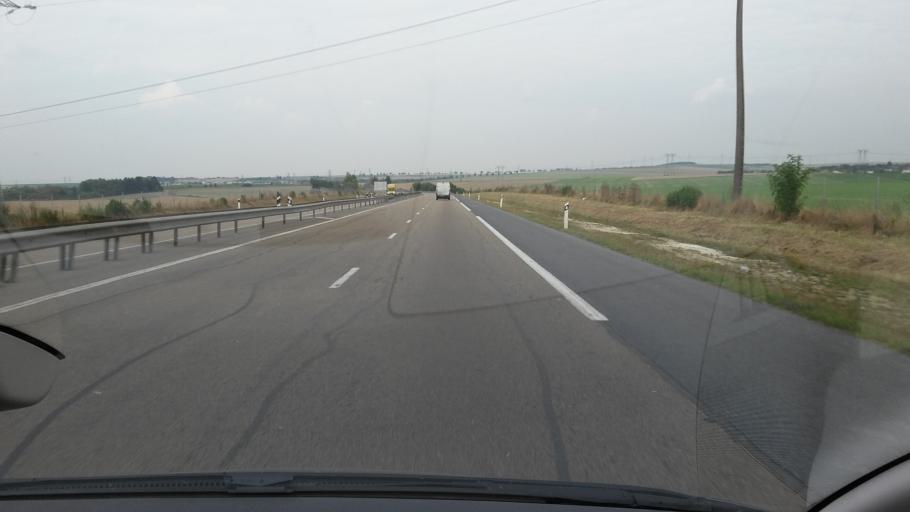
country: FR
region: Champagne-Ardenne
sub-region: Departement de la Marne
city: Cernay-les-Reims
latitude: 49.2523
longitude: 4.0841
